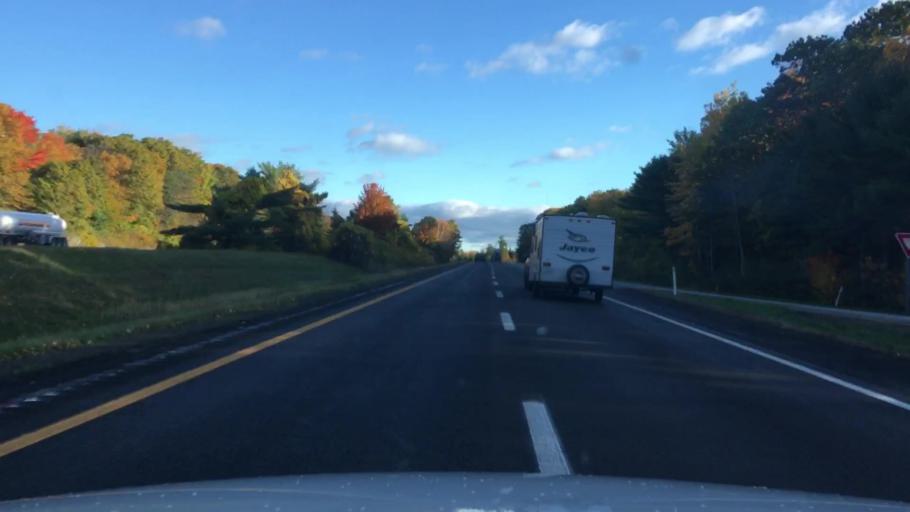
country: US
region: Maine
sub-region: Penobscot County
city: Orono
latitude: 44.8742
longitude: -68.7013
